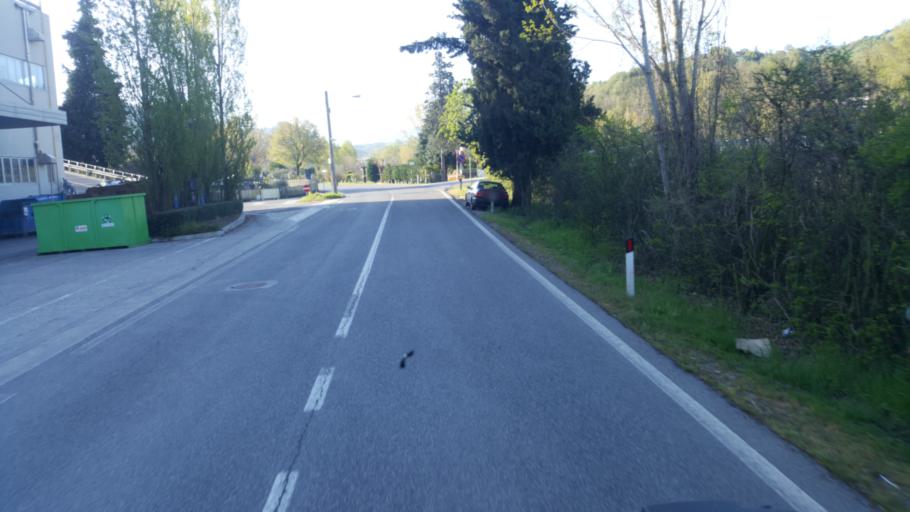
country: SM
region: Acquaviva
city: Acquaviva
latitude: 43.9423
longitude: 12.4064
